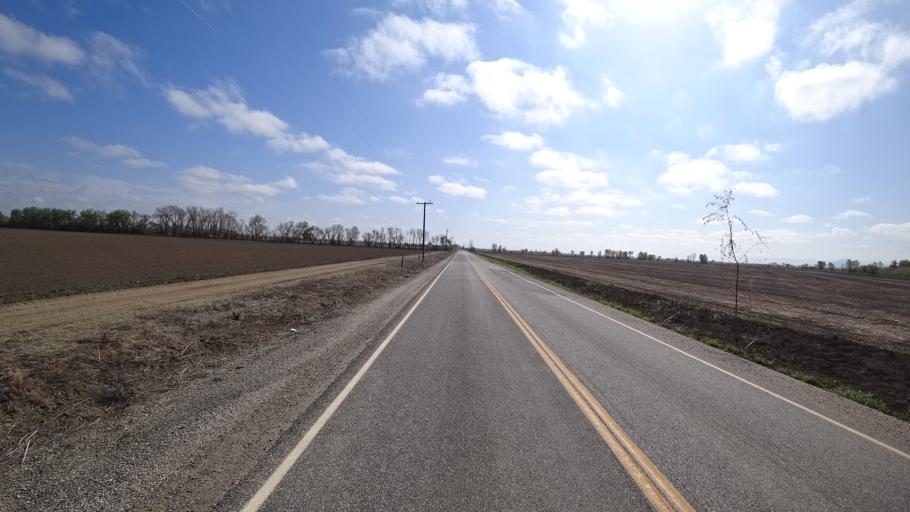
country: US
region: California
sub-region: Colusa County
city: Colusa
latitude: 39.3912
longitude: -121.9355
